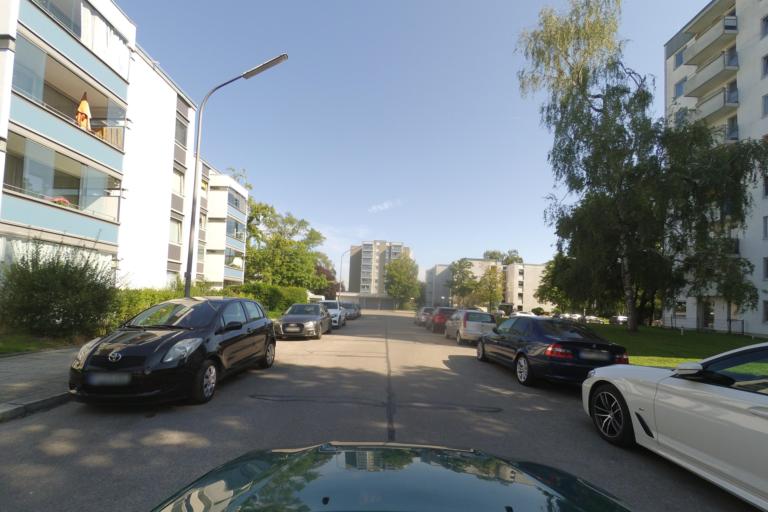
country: DE
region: Bavaria
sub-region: Upper Bavaria
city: Neuried
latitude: 48.0937
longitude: 11.4785
